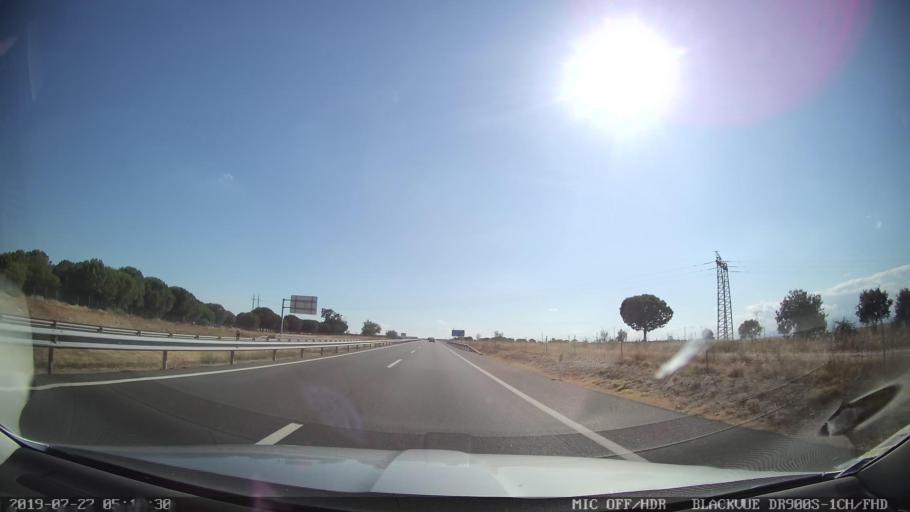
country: ES
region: Castille-La Mancha
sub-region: Province of Toledo
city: Maqueda
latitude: 40.0472
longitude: -4.3934
